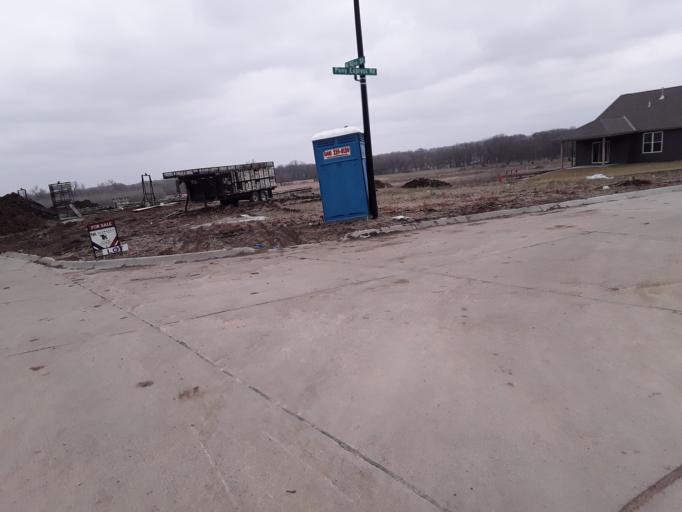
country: US
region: Nebraska
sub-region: Lancaster County
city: Lincoln
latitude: 40.8457
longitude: -96.5954
